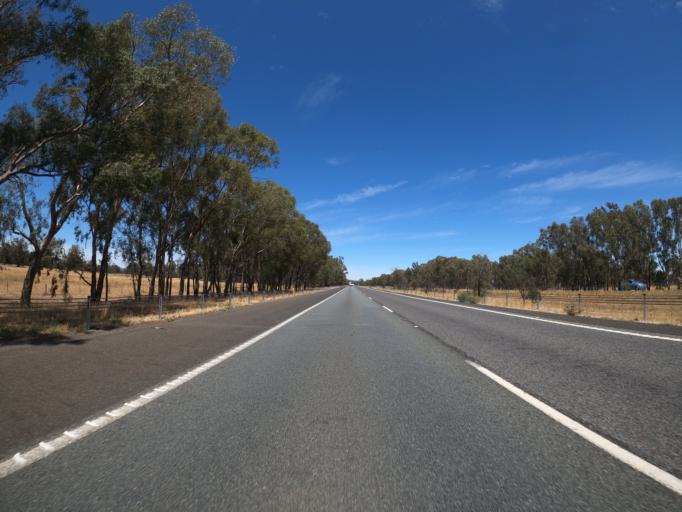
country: AU
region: Victoria
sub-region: Benalla
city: Benalla
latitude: -36.5935
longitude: 145.8876
